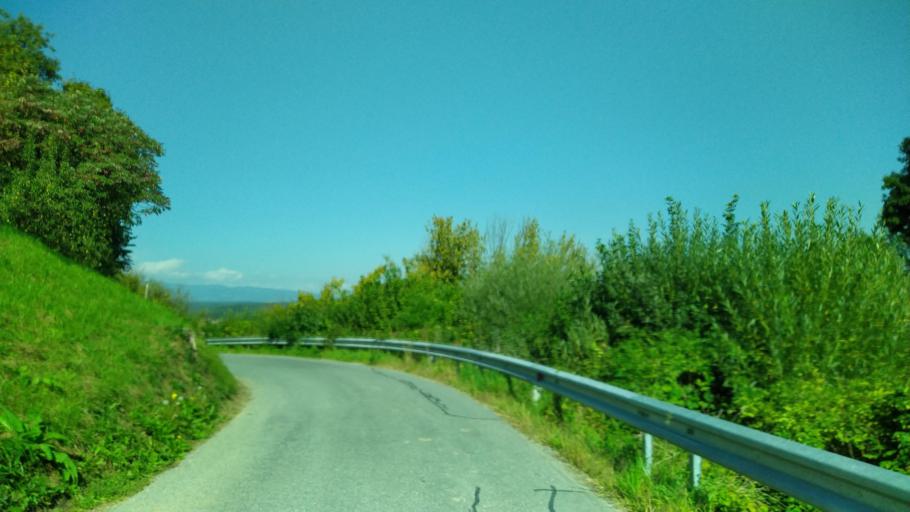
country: AT
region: Styria
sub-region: Politischer Bezirk Deutschlandsberg
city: Wettmannstatten
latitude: 46.8241
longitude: 15.3679
